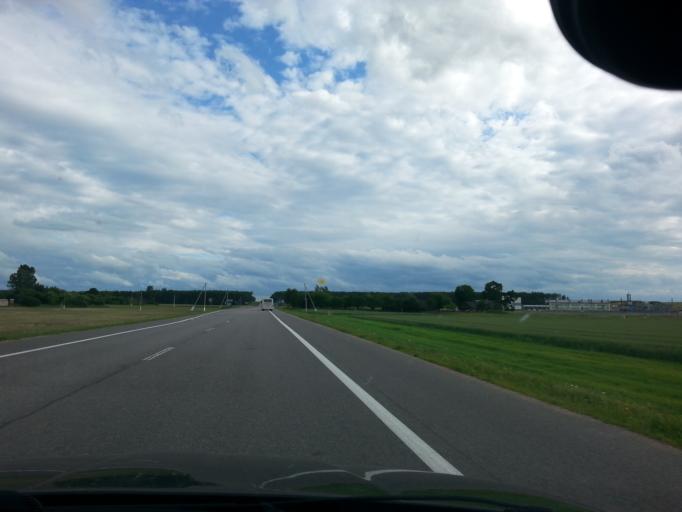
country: BY
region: Grodnenskaya
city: Astravyets
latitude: 54.7144
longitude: 26.0824
